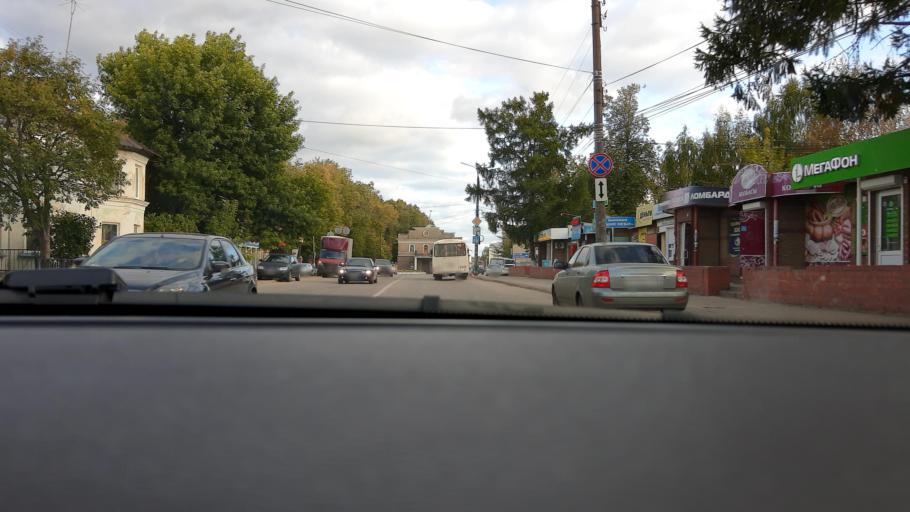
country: RU
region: Nizjnij Novgorod
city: Novaya Balakhna
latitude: 56.4937
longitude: 43.6098
